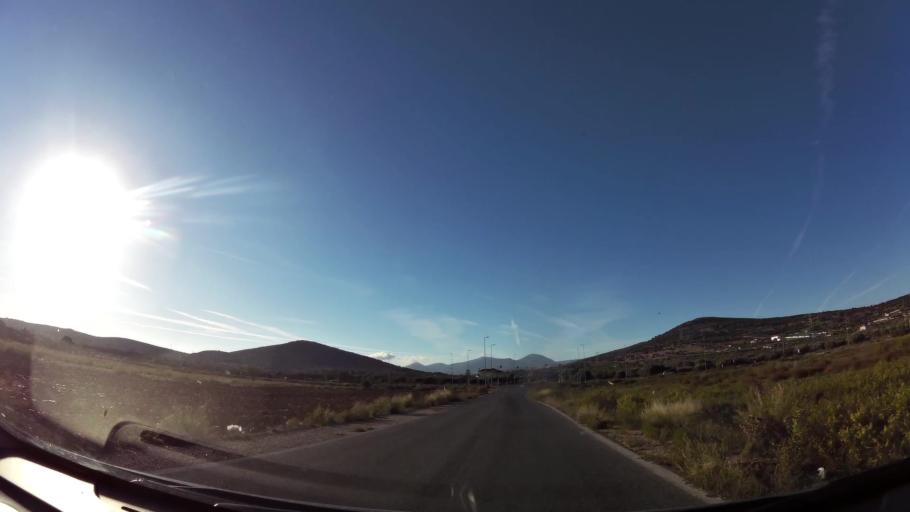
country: GR
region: Attica
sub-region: Nomarchia Anatolikis Attikis
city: Kalyvia Thorikou
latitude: 37.8490
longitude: 23.9152
